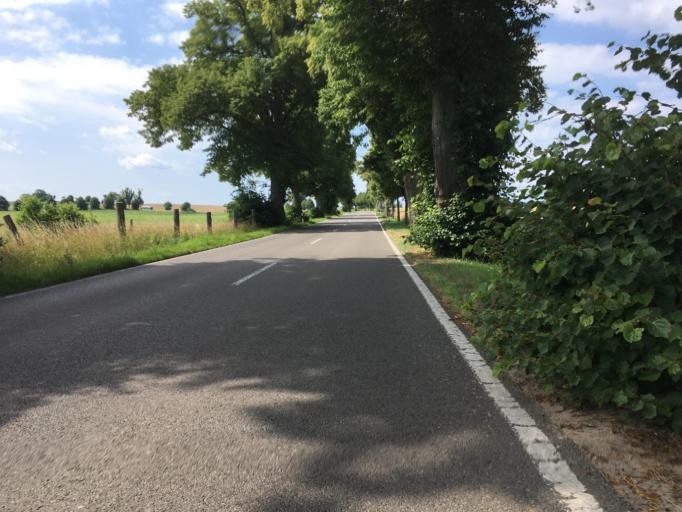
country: DE
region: Brandenburg
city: Friedrichswalde
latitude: 53.0461
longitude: 13.7116
